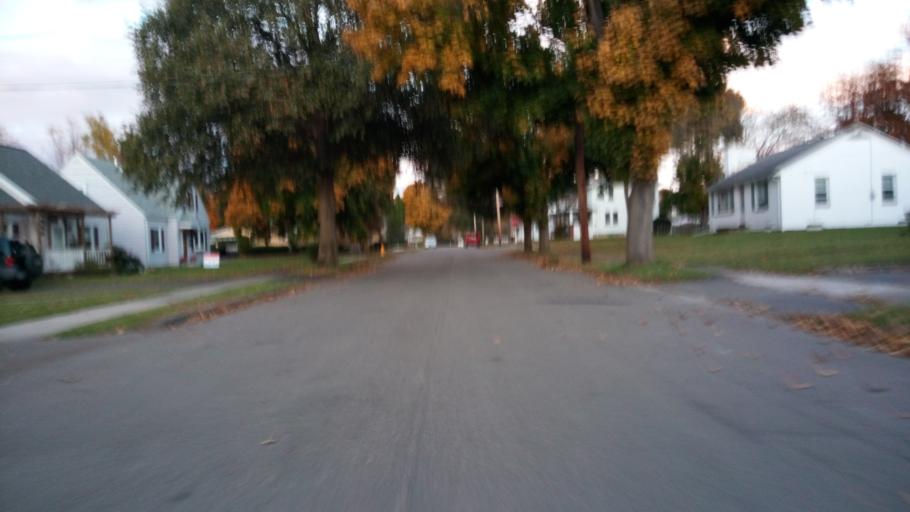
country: US
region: New York
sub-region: Chemung County
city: Elmira
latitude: 42.0784
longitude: -76.8165
